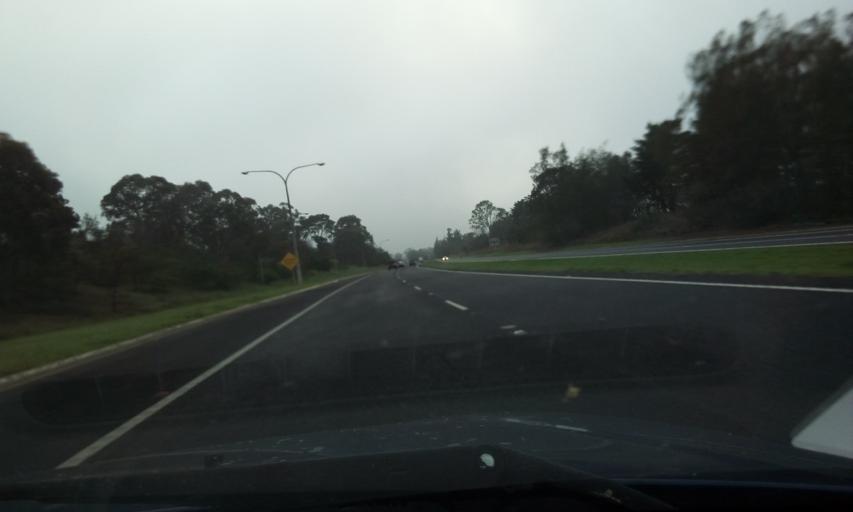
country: AU
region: New South Wales
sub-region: Camden
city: Elderslie
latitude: -34.0649
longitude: 150.7152
